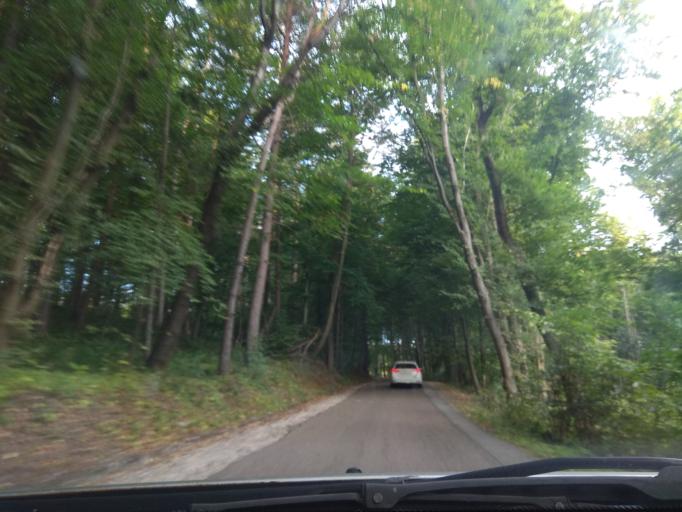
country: HU
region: Borsod-Abauj-Zemplen
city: Saly
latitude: 48.0704
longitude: 20.6545
